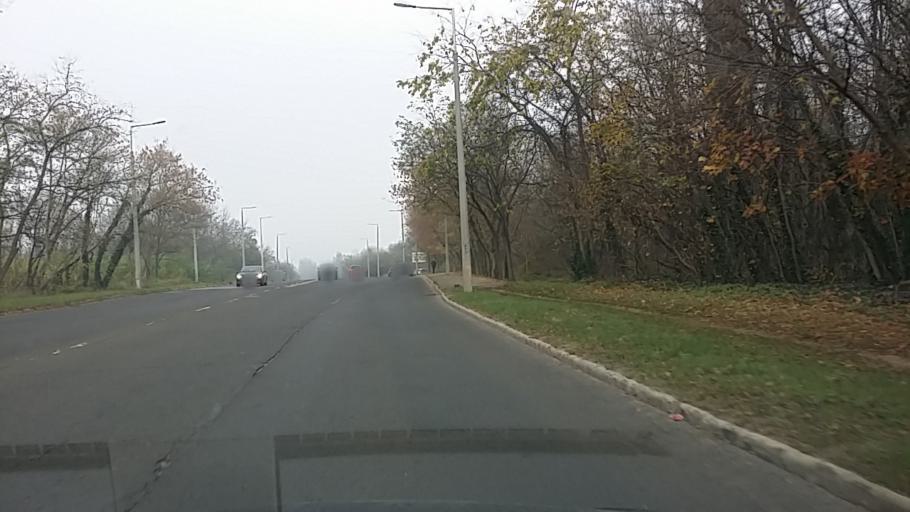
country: HU
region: Budapest
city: Budapest XV. keruelet
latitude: 47.5838
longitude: 19.1045
